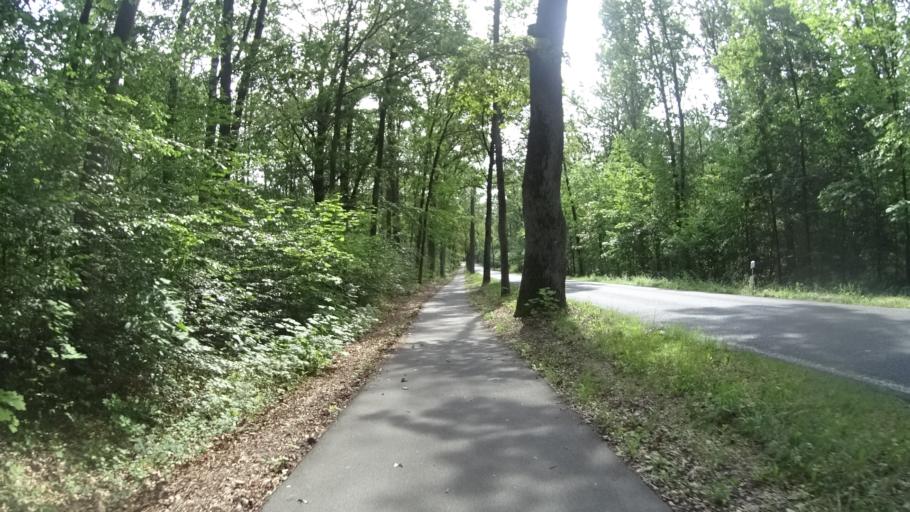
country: DE
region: Brandenburg
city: Gross Kreutz
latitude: 52.3115
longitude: 12.7516
